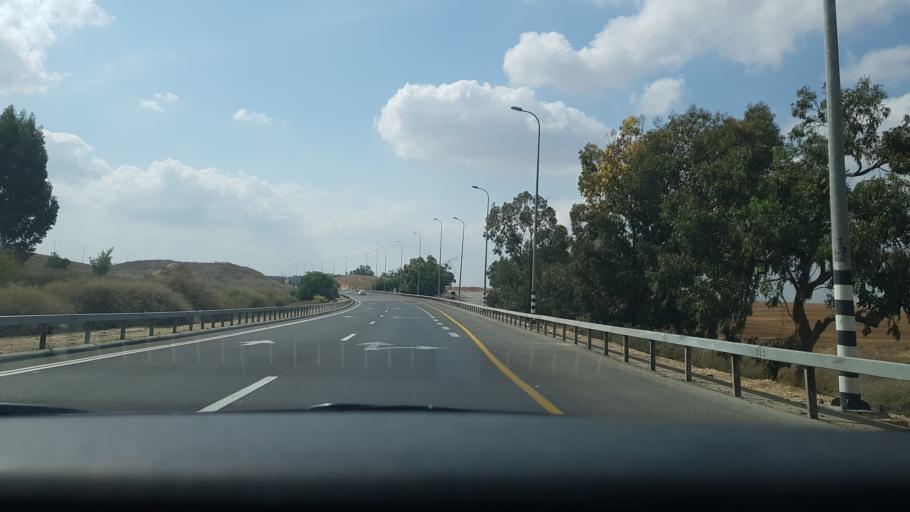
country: IL
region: Southern District
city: Qiryat Gat
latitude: 31.4959
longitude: 34.7806
